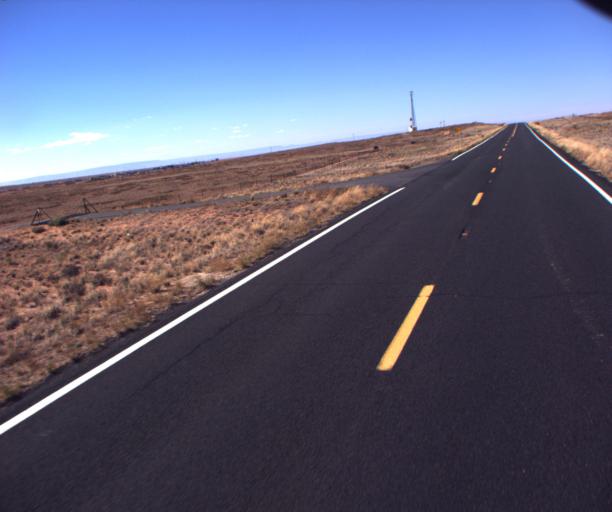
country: US
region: Arizona
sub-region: Coconino County
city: Tuba City
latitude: 35.9916
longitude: -111.0147
